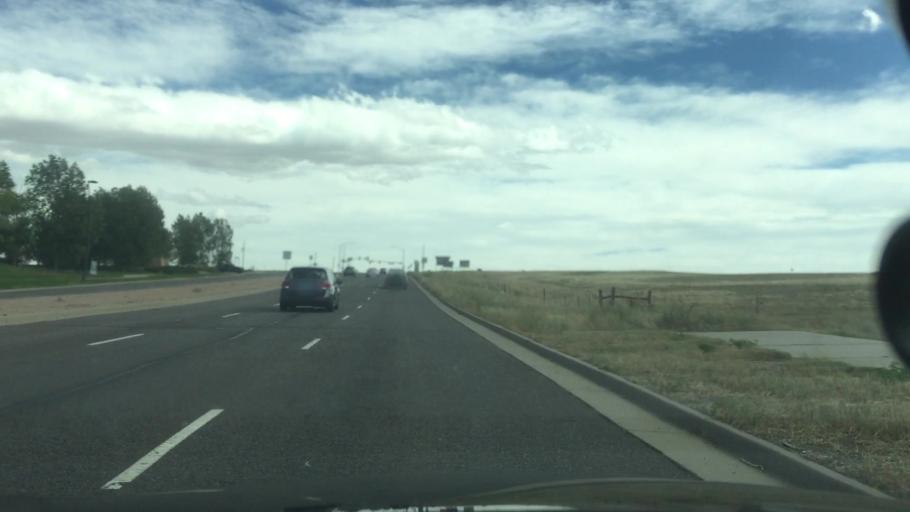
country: US
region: Colorado
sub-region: Arapahoe County
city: Dove Valley
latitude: 39.6529
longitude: -104.7392
